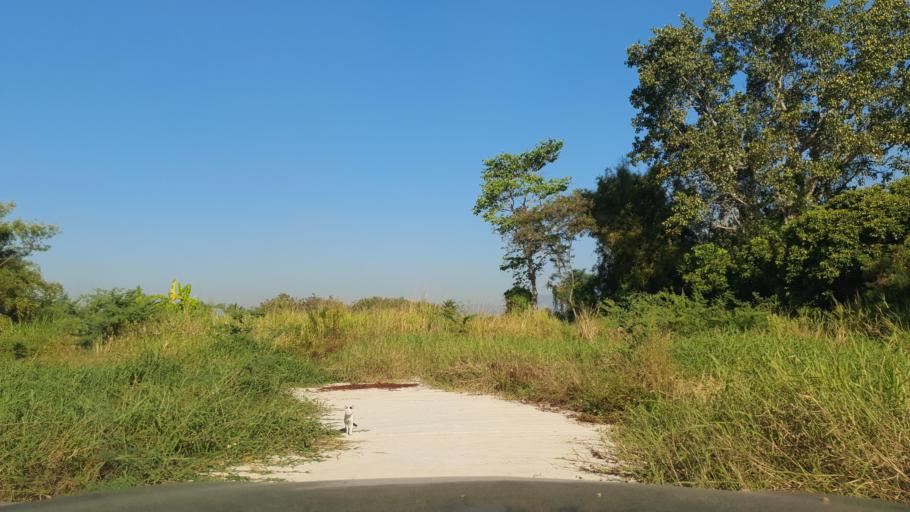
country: TH
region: Chiang Mai
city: Hang Dong
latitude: 18.6926
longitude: 98.9414
